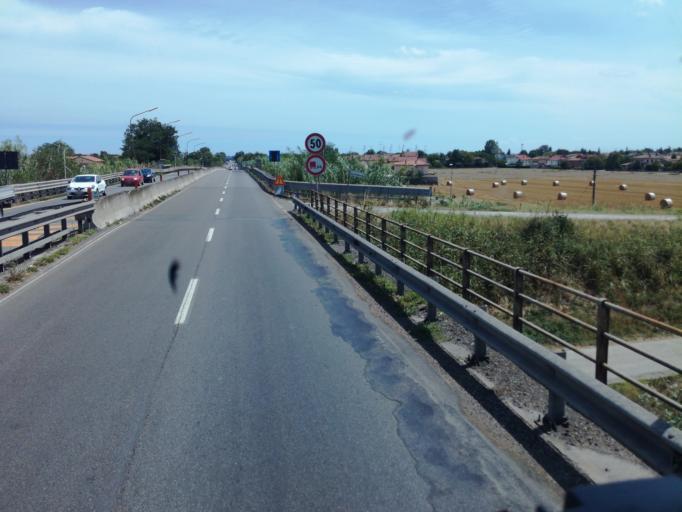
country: IT
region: Emilia-Romagna
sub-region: Provincia di Ravenna
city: Madonna Dell'Albero
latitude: 44.3842
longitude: 12.1955
